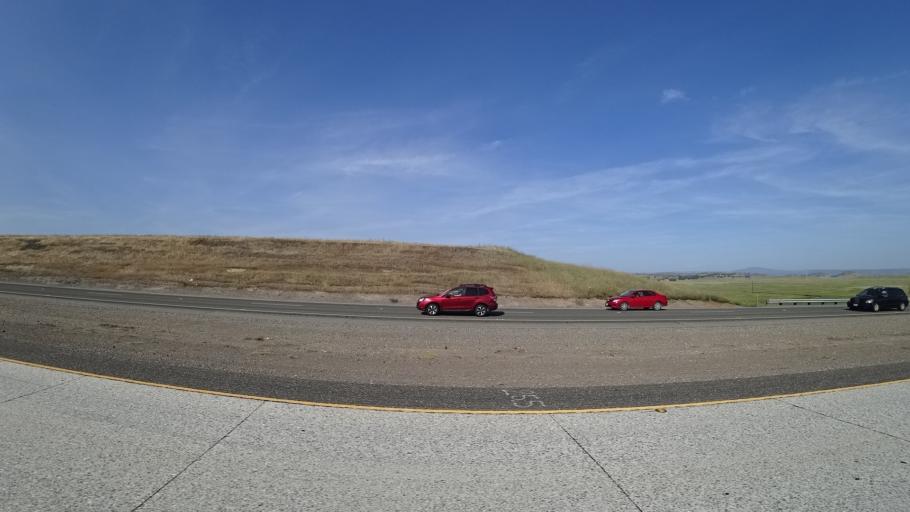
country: US
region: California
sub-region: Butte County
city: Durham
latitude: 39.6600
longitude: -121.7365
